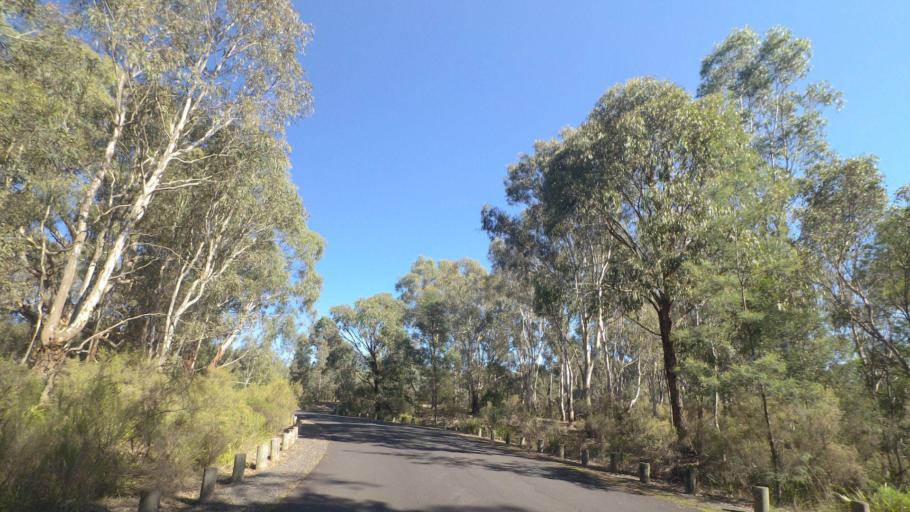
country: AU
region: Victoria
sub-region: Banyule
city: Darch
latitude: -37.7486
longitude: 145.1348
